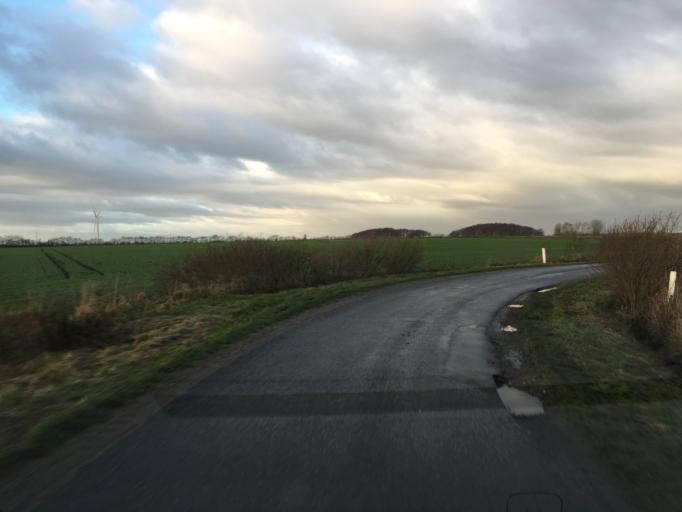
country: DK
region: South Denmark
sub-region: Tonder Kommune
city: Sherrebek
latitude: 55.1425
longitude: 8.8248
